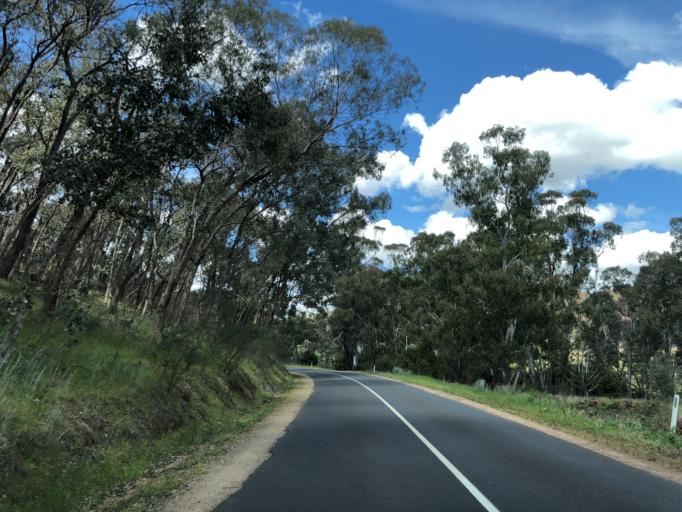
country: AU
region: Victoria
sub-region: Benalla
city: Benalla
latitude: -36.7568
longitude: 146.1204
